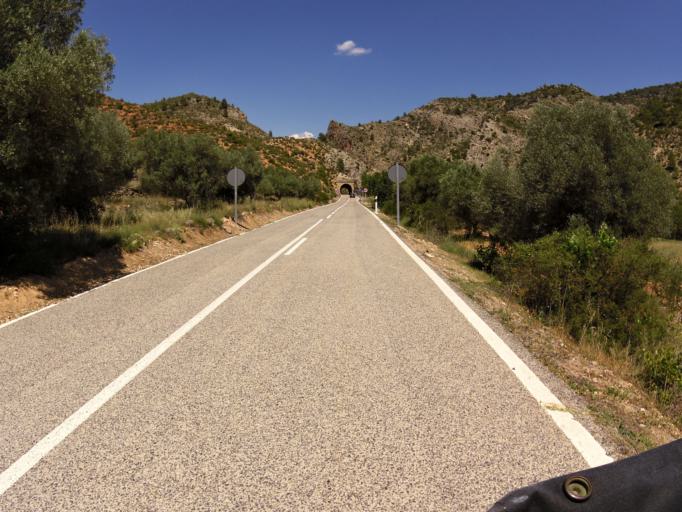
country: ES
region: Valencia
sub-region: Provincia de Valencia
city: Casas Bajas
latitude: 40.0057
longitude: -1.2749
